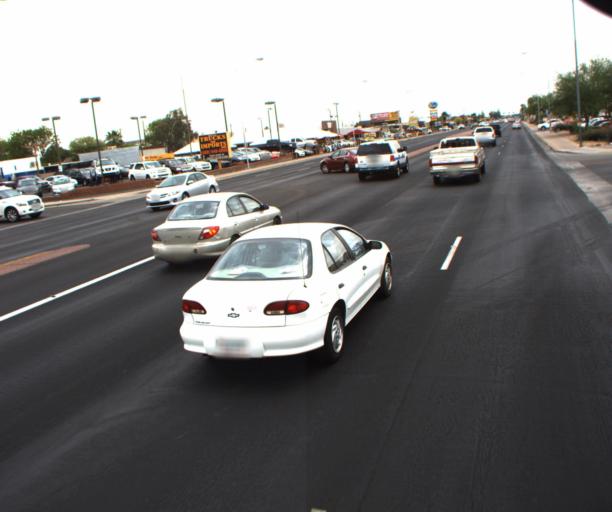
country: US
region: Arizona
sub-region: Maricopa County
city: Mesa
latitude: 33.3972
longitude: -111.8402
